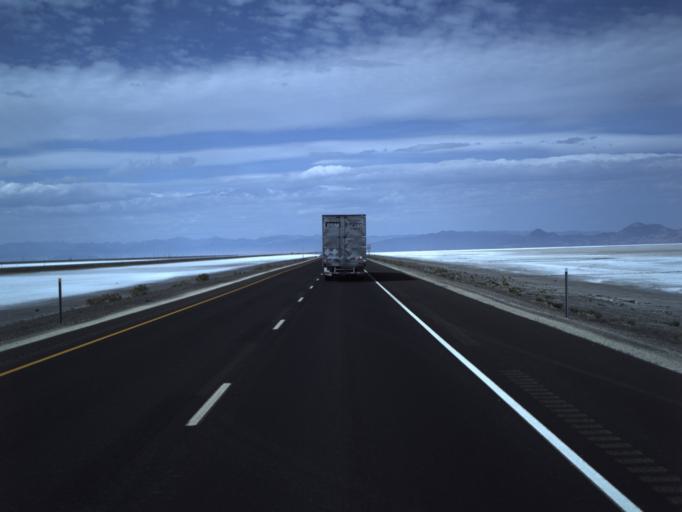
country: US
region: Utah
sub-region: Tooele County
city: Wendover
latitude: 40.7353
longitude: -113.6534
